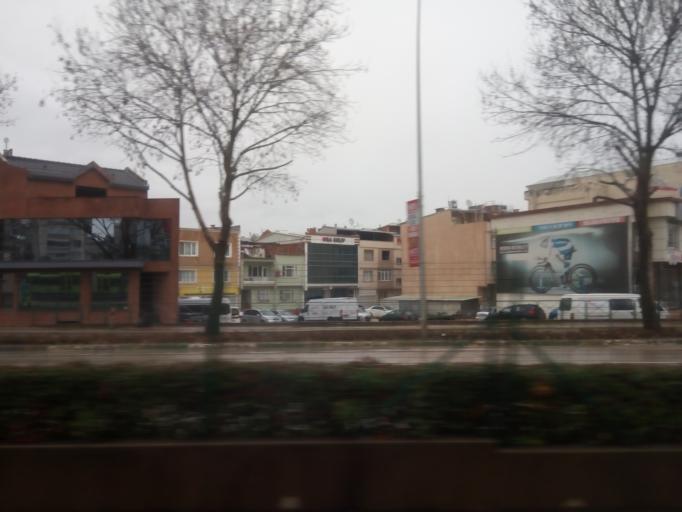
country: TR
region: Bursa
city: Yildirim
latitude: 40.2247
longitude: 28.9922
